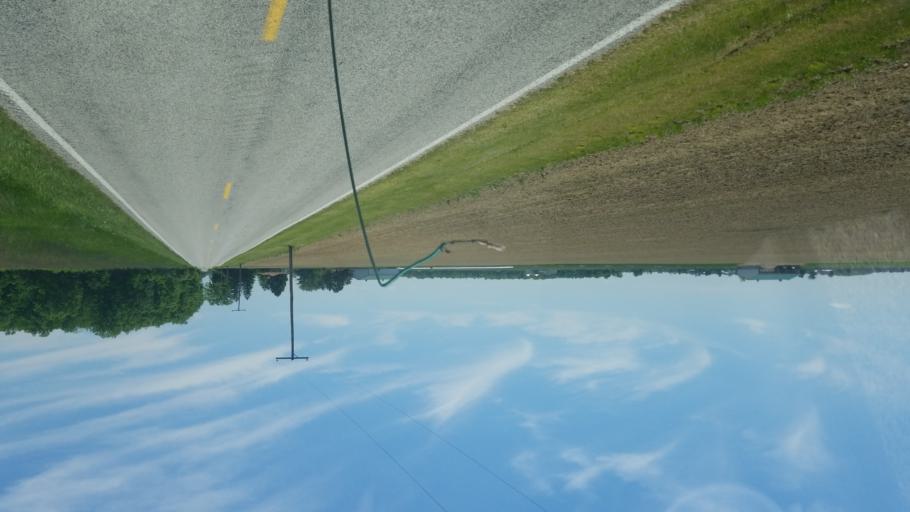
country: US
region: Ohio
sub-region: Huron County
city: Norwalk
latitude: 41.1892
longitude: -82.5528
